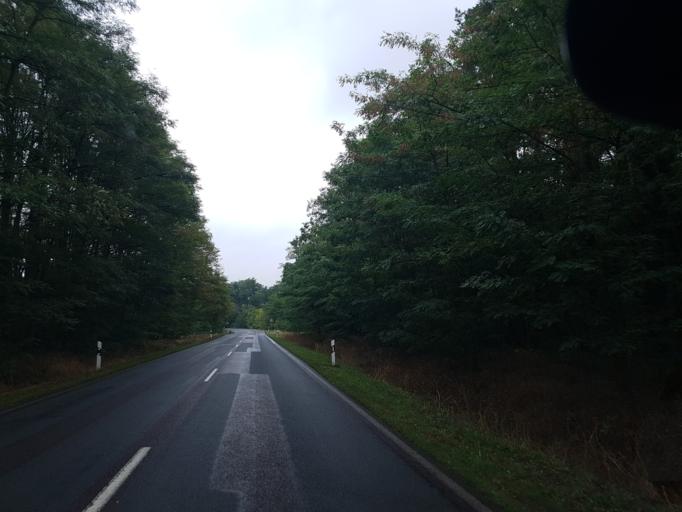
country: DE
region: Saxony-Anhalt
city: Tucheim
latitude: 52.2693
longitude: 12.1595
